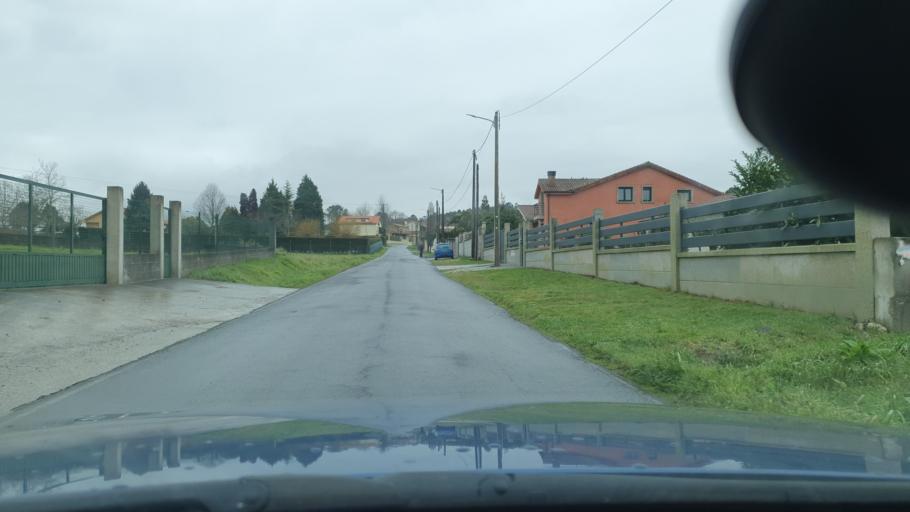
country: ES
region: Galicia
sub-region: Provincia da Coruna
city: Ames
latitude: 42.8310
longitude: -8.6077
